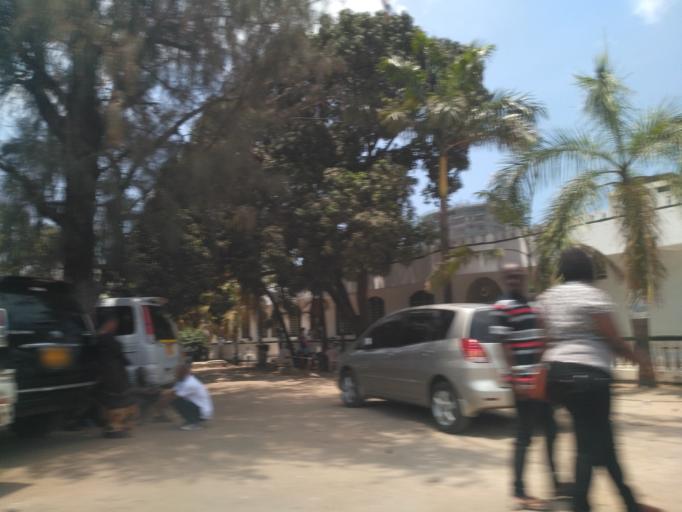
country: TZ
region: Dar es Salaam
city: Dar es Salaam
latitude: -6.8028
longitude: 39.2732
